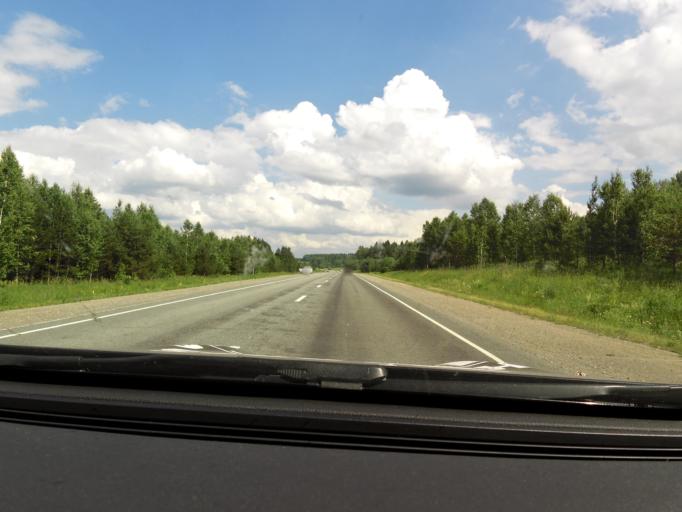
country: RU
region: Sverdlovsk
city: Arti
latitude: 56.7966
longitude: 58.6423
